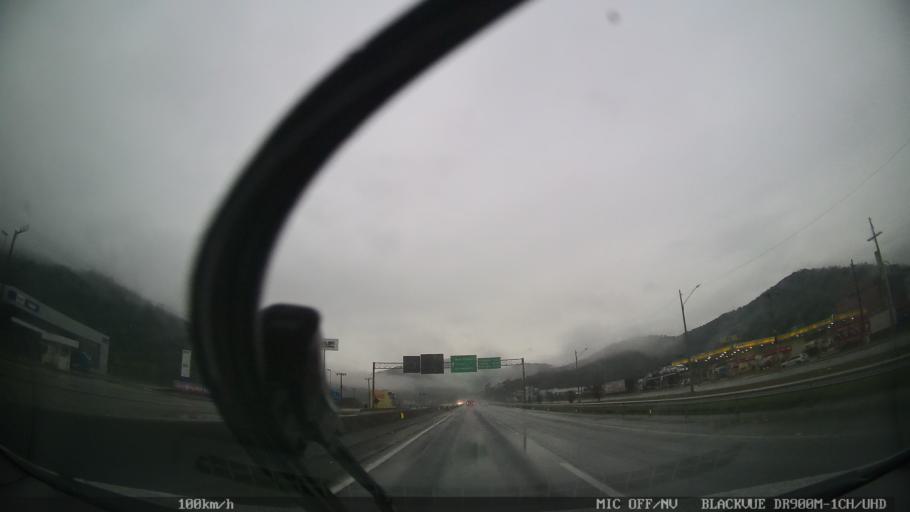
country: BR
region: Santa Catarina
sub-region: Itajai
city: Itajai
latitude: -26.9461
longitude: -48.6872
